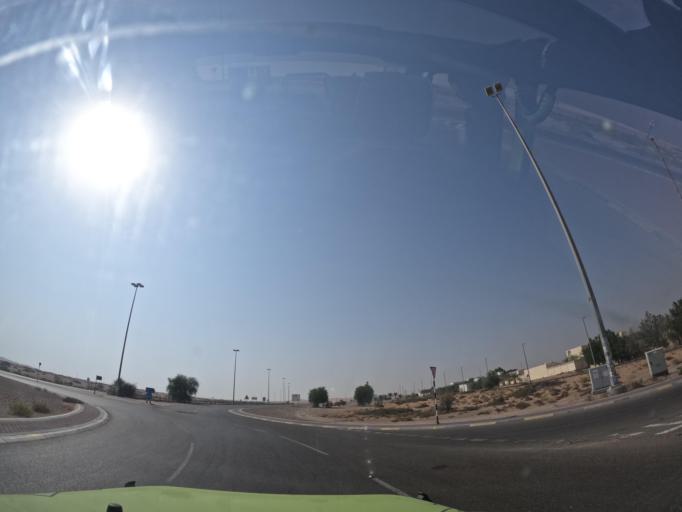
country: OM
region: Al Buraimi
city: Al Buraymi
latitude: 24.5242
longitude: 55.5528
